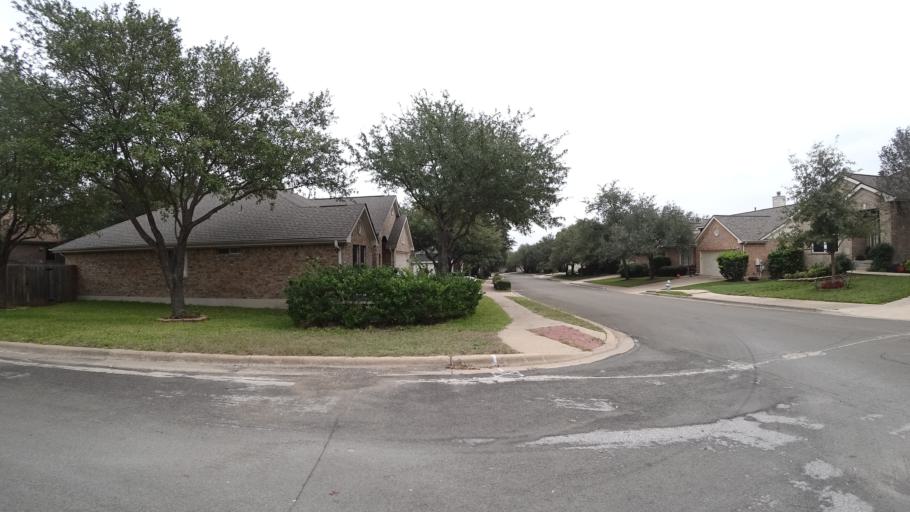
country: US
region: Texas
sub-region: Travis County
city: Shady Hollow
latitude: 30.2132
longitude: -97.8891
